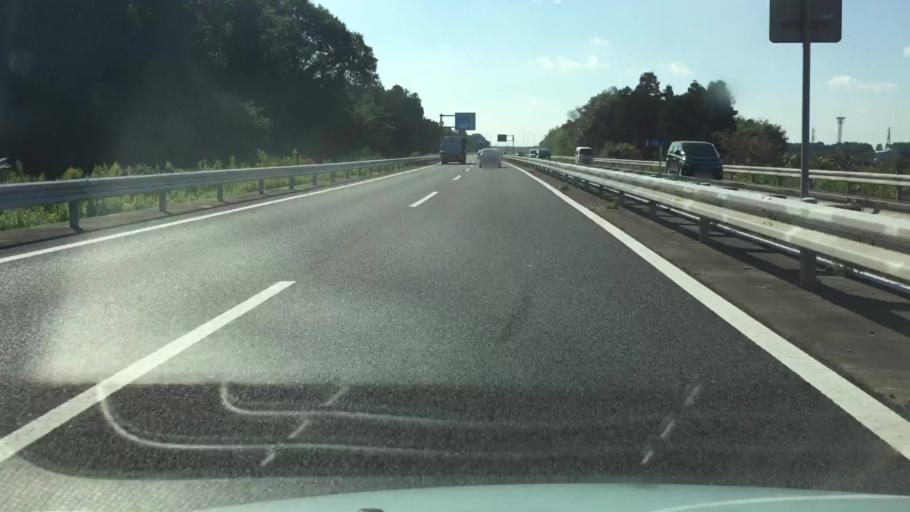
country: JP
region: Tochigi
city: Mooka
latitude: 36.4973
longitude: 139.9899
